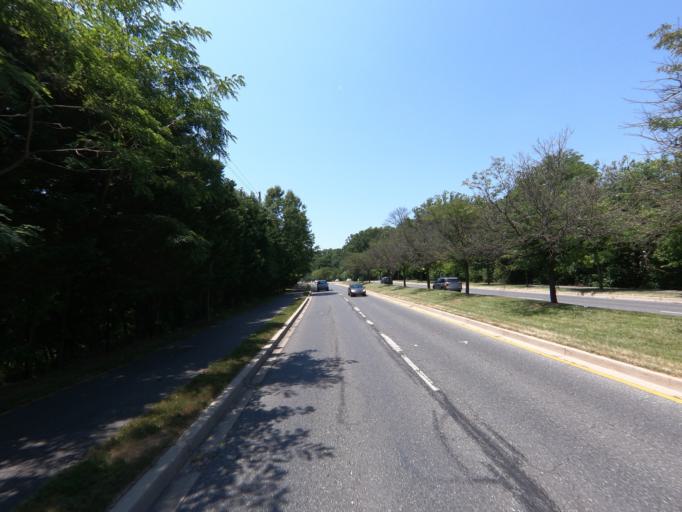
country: US
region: Maryland
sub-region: Montgomery County
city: Olney
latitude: 39.1481
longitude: -77.0539
